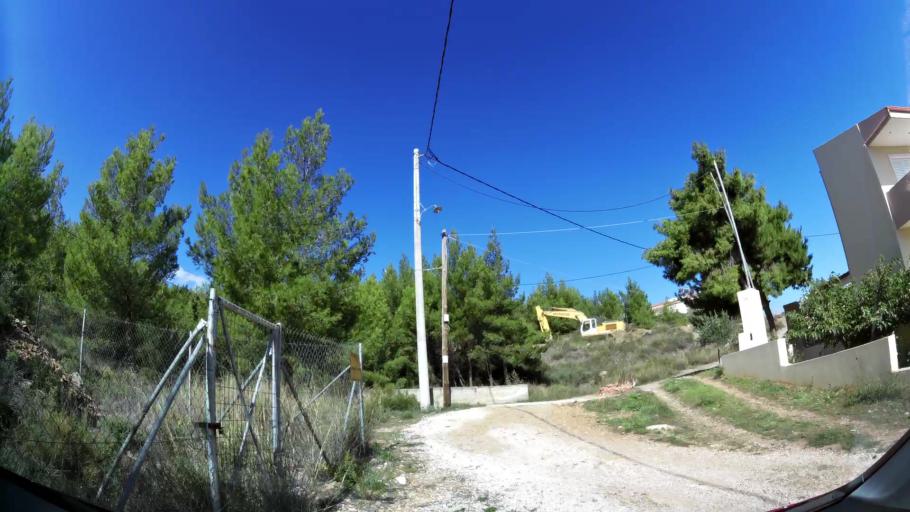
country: GR
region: Attica
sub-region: Nomarchia Anatolikis Attikis
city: Dioni
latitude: 38.0350
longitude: 23.9400
